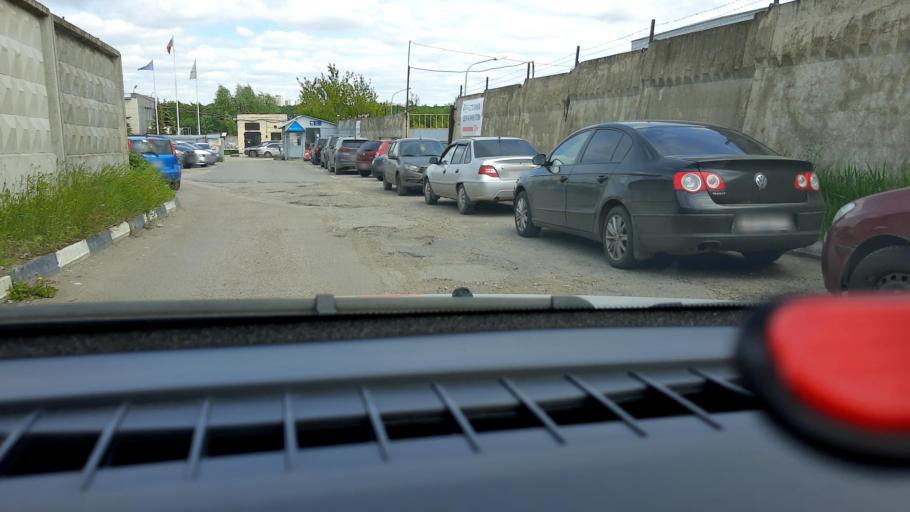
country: RU
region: Nizjnij Novgorod
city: Nizhniy Novgorod
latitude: 56.2415
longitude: 44.0027
